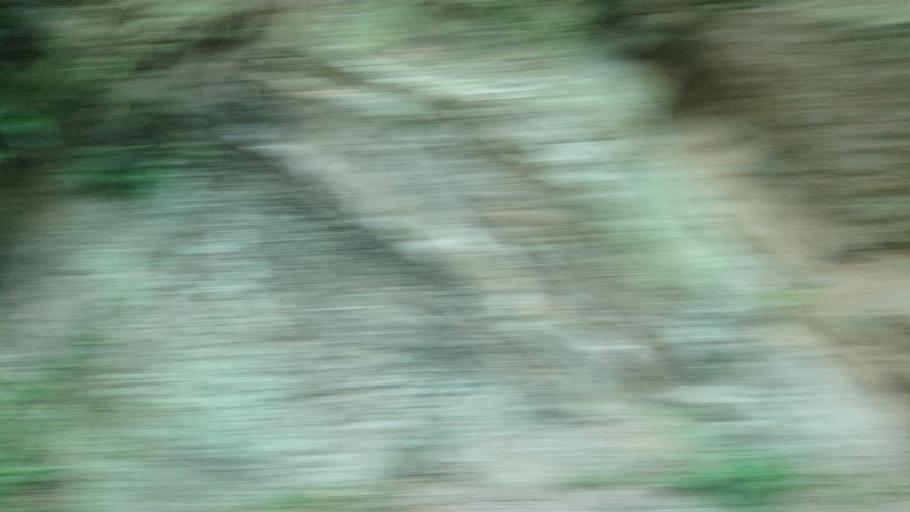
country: TW
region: Taiwan
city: Daxi
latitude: 24.8875
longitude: 121.3769
